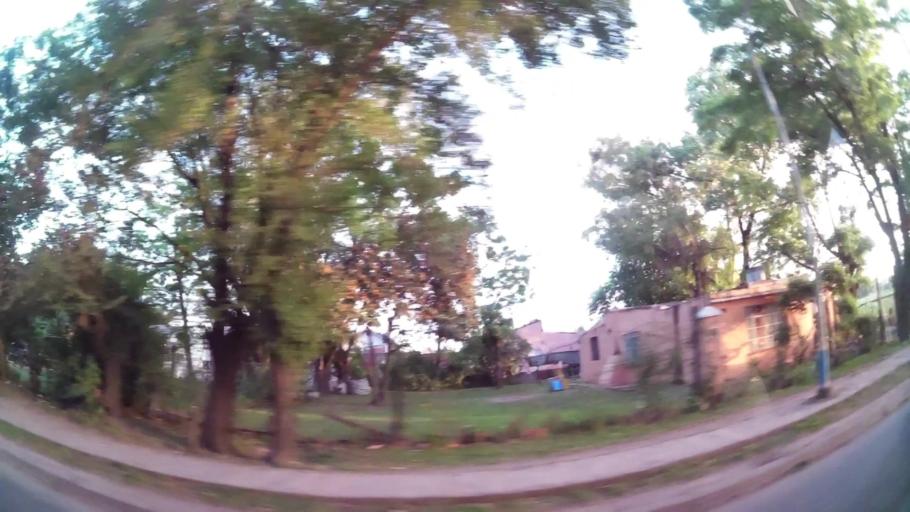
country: AR
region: Buenos Aires
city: Santa Catalina - Dique Lujan
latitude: -34.4879
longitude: -58.7510
